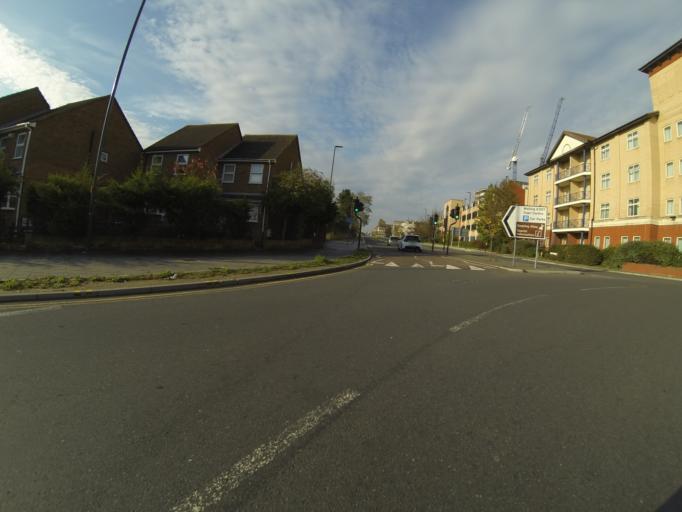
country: GB
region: England
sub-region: Greater London
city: Bexley
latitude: 51.4543
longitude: 0.1523
